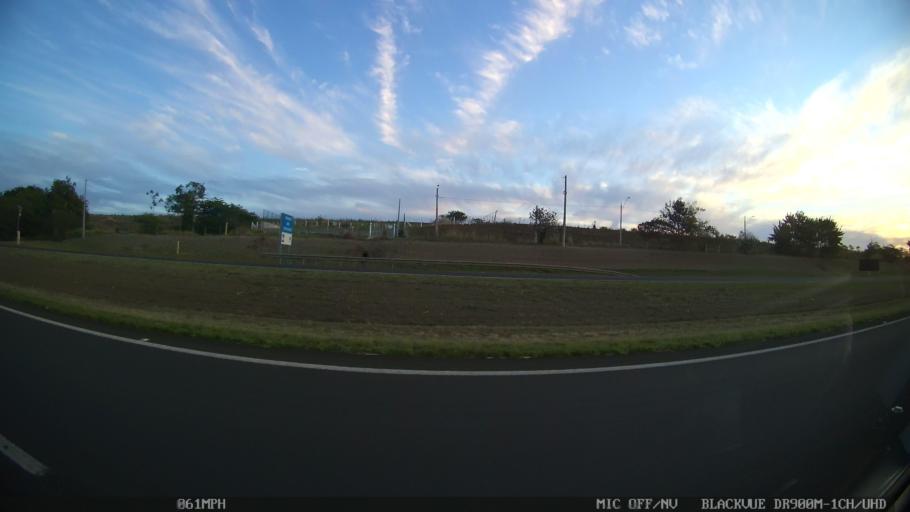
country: BR
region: Sao Paulo
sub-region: Catanduva
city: Catanduva
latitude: -21.1672
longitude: -48.9768
